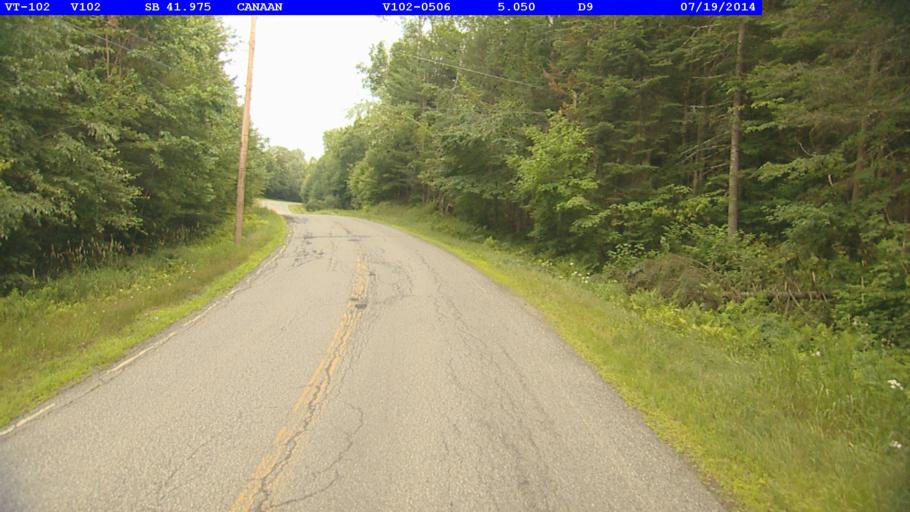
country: US
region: New Hampshire
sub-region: Coos County
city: Colebrook
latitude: 44.9736
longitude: -71.5350
